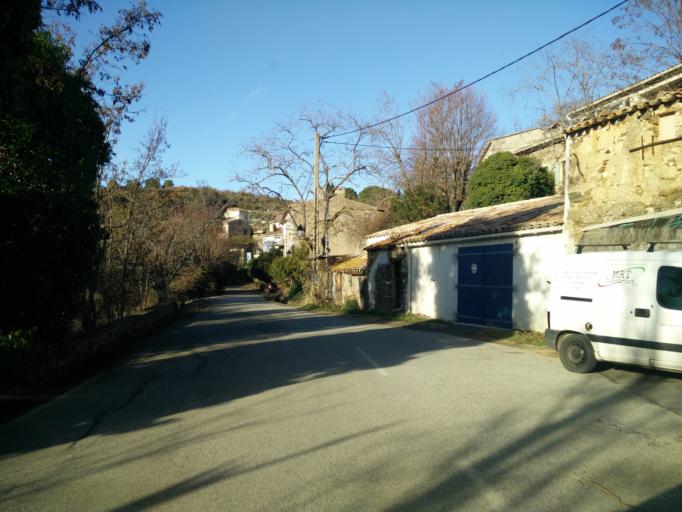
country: FR
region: Provence-Alpes-Cote d'Azur
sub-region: Departement du Var
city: La Garde-Freinet
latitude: 43.3427
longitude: 6.4911
